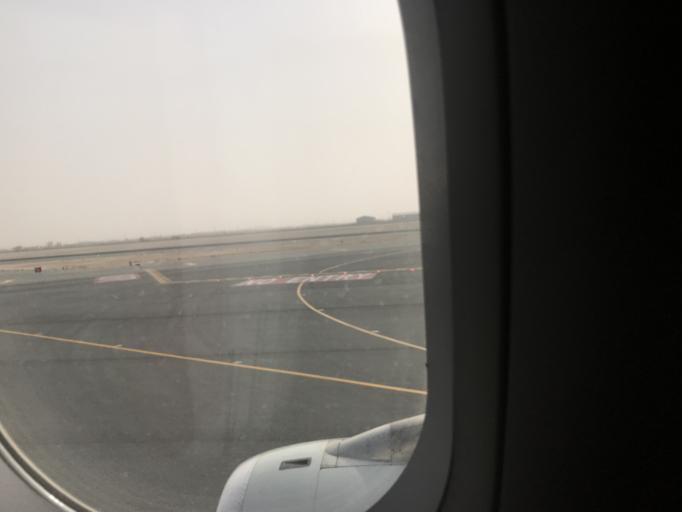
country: QA
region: Baladiyat ad Dawhah
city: Doha
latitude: 25.2724
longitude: 51.5999
